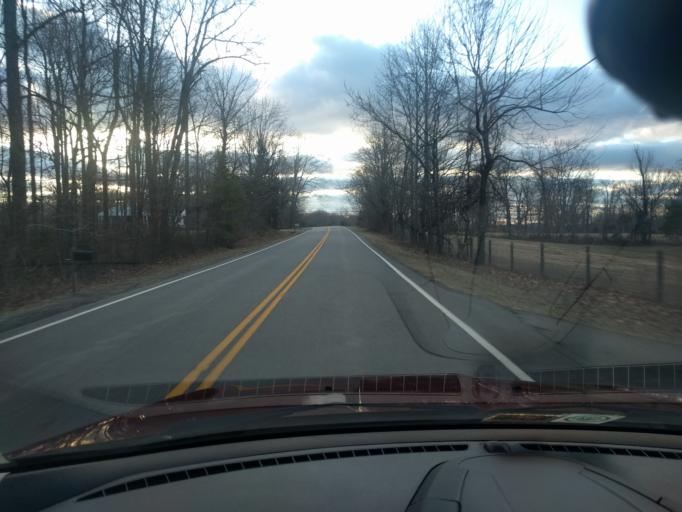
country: US
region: Virginia
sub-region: City of Bedford
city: Bedford
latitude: 37.4097
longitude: -79.5632
